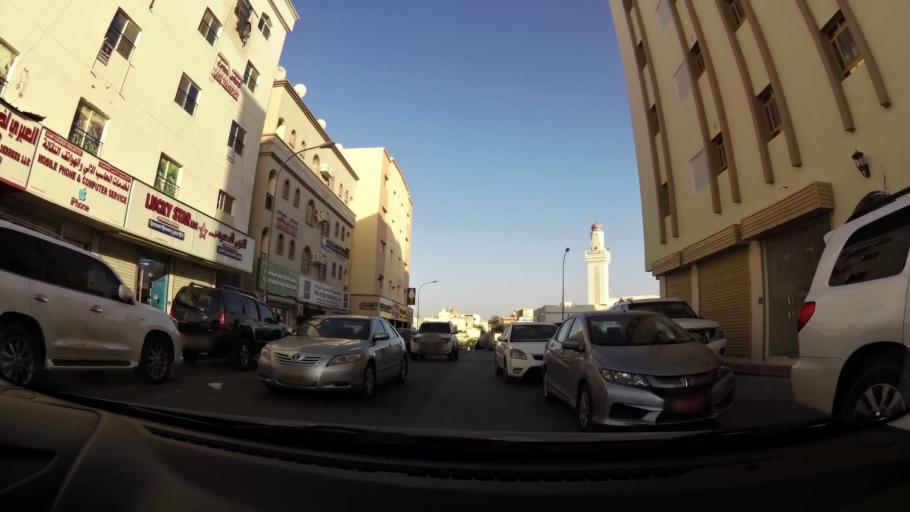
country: OM
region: Muhafazat Masqat
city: As Sib al Jadidah
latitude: 23.6069
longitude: 58.2260
